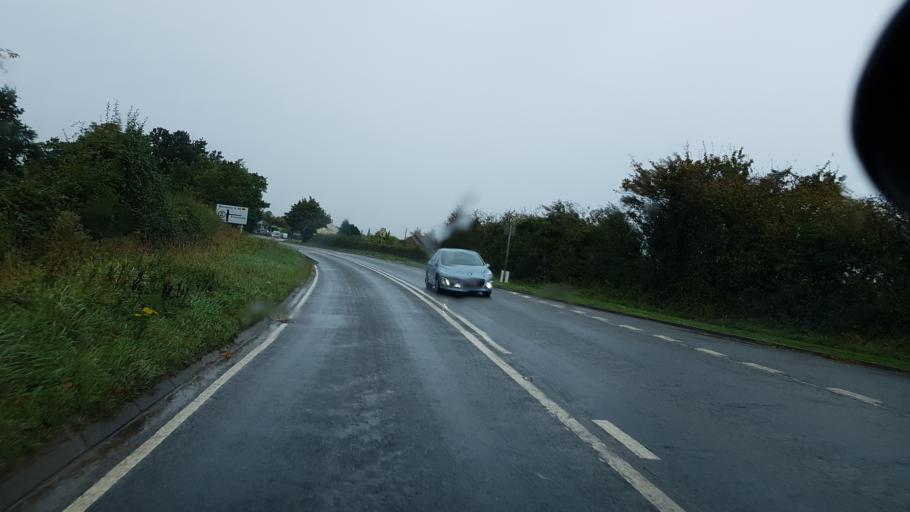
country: GB
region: England
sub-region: Worcestershire
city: Upton upon Severn
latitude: 52.0615
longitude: -2.1934
